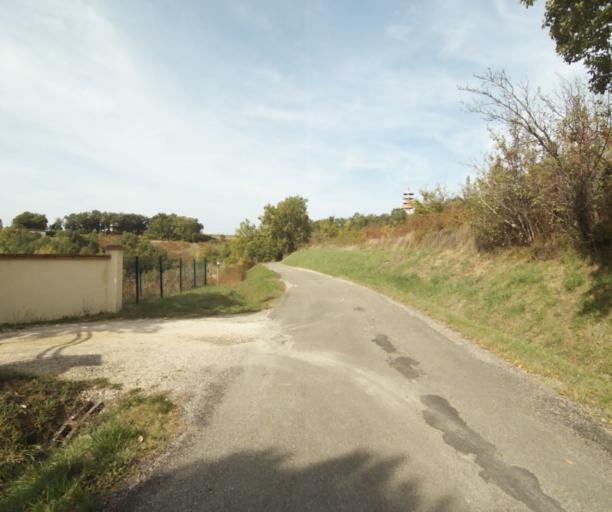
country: FR
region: Midi-Pyrenees
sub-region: Departement du Tarn-et-Garonne
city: Corbarieu
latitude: 43.9633
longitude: 1.3784
